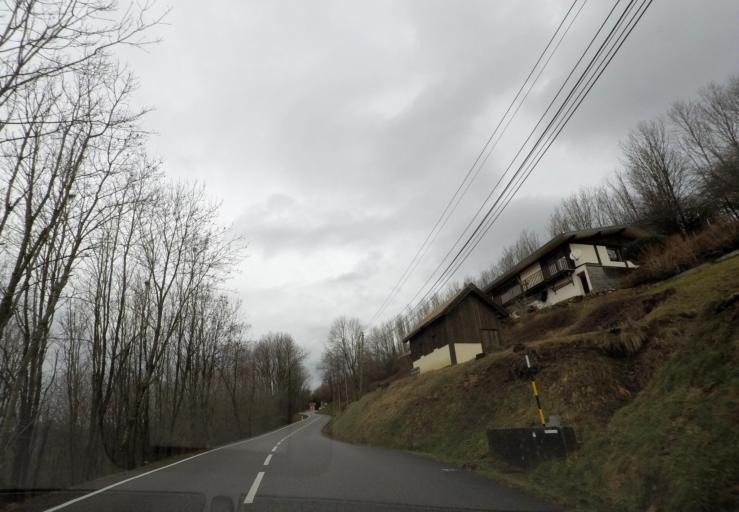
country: FR
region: Rhone-Alpes
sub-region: Departement de la Haute-Savoie
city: Chatillon-sur-Cluses
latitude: 46.0735
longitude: 6.6141
